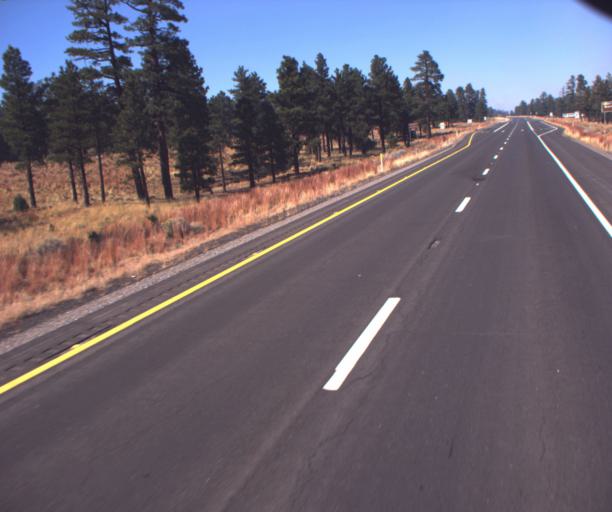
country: US
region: Arizona
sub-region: Coconino County
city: Flagstaff
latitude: 35.3701
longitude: -111.5741
